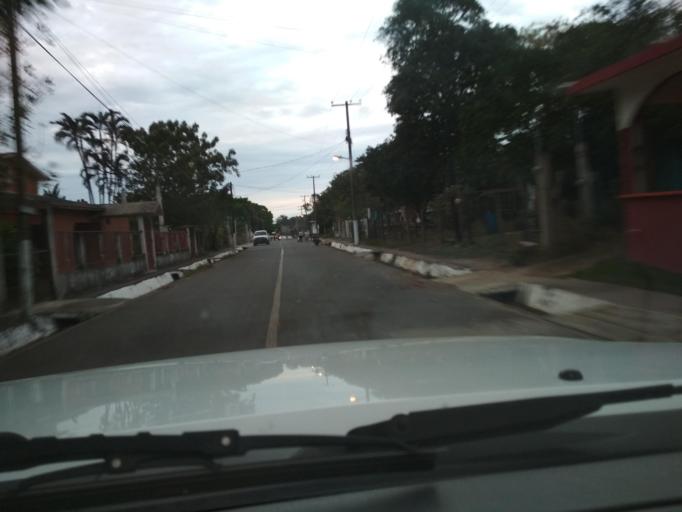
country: MX
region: Veracruz
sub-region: Veracruz
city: Delfino Victoria (Santa Fe)
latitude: 19.1614
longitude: -96.2602
